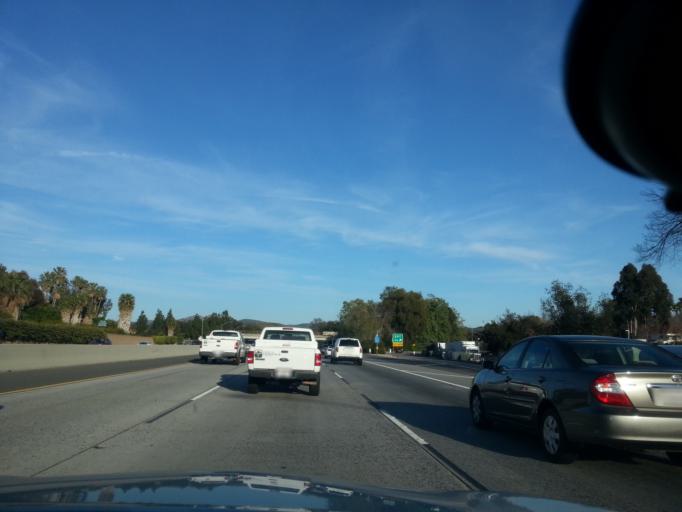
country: US
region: California
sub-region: Ventura County
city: Casa Conejo
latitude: 34.1843
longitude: -118.9150
